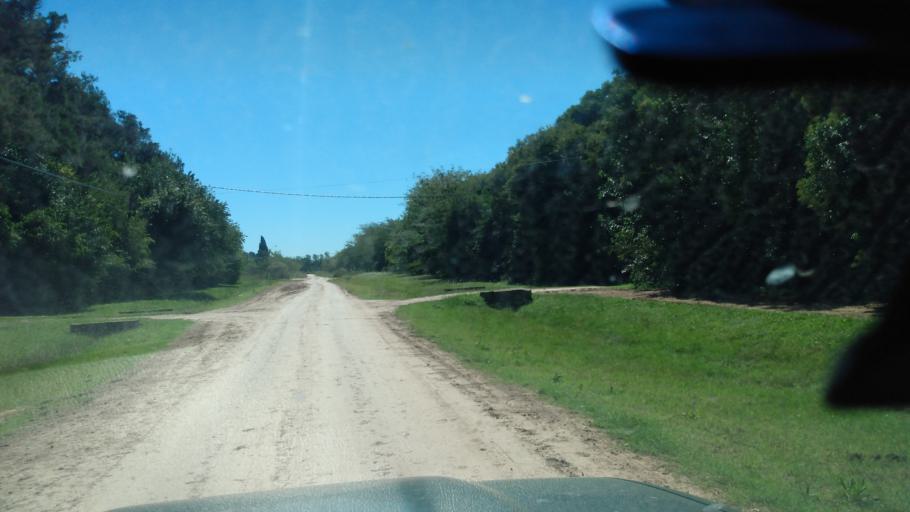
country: AR
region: Buenos Aires
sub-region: Partido de Lujan
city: Lujan
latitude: -34.5535
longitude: -59.1445
